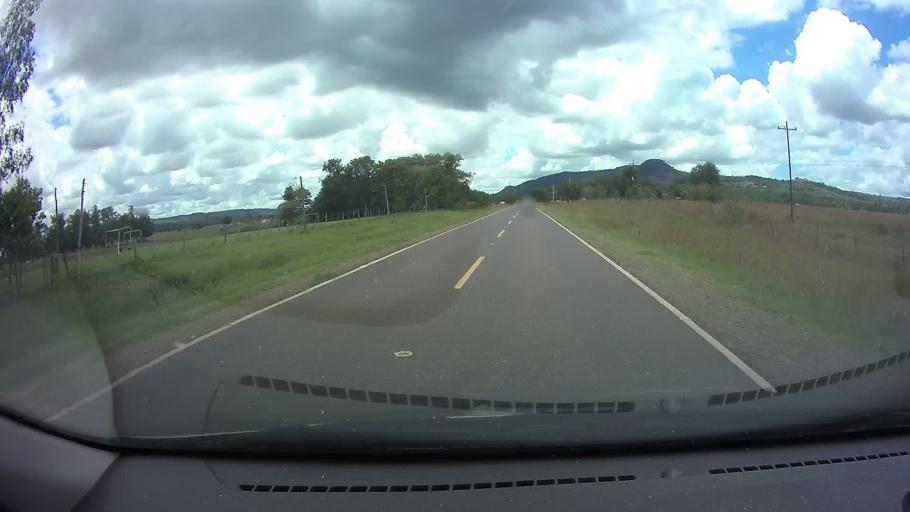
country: PY
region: Paraguari
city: Ybycui
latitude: -25.9100
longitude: -57.0010
